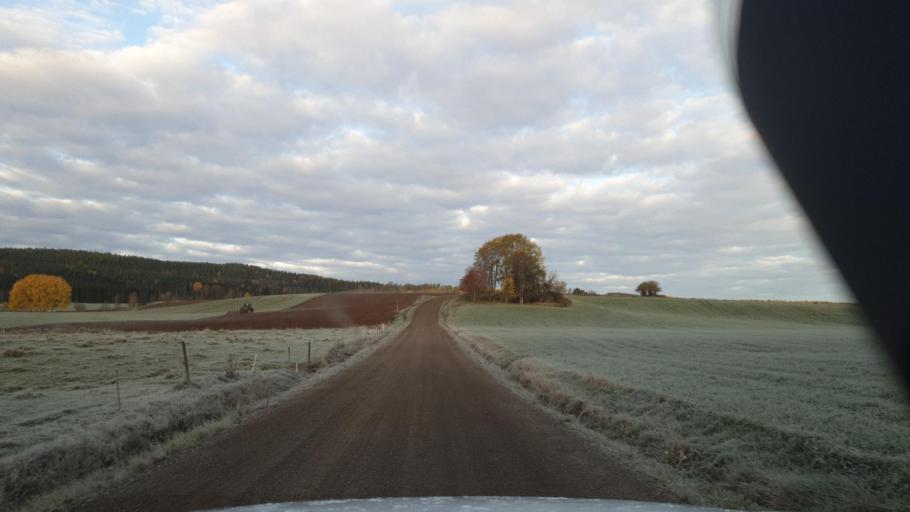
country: SE
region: Vaermland
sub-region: Eda Kommun
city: Amotfors
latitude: 59.7212
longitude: 12.1566
